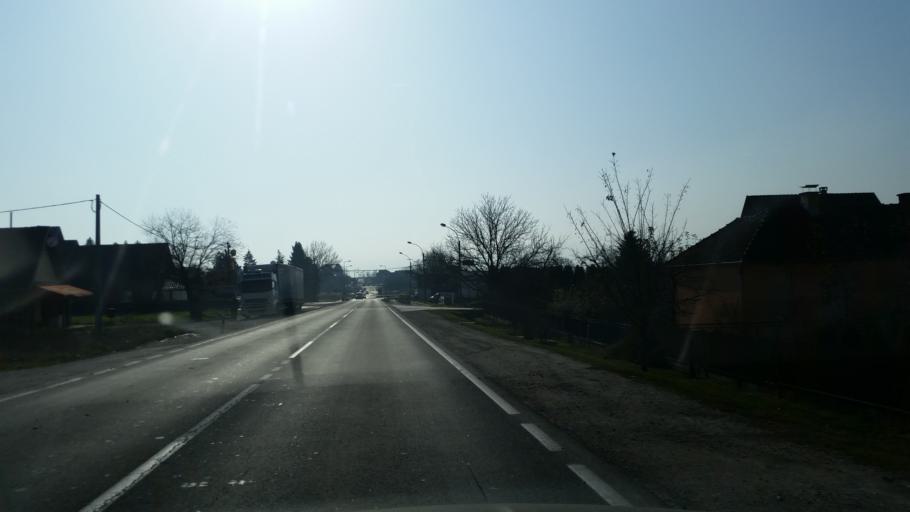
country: RS
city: Prislonica
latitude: 43.9214
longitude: 20.4087
